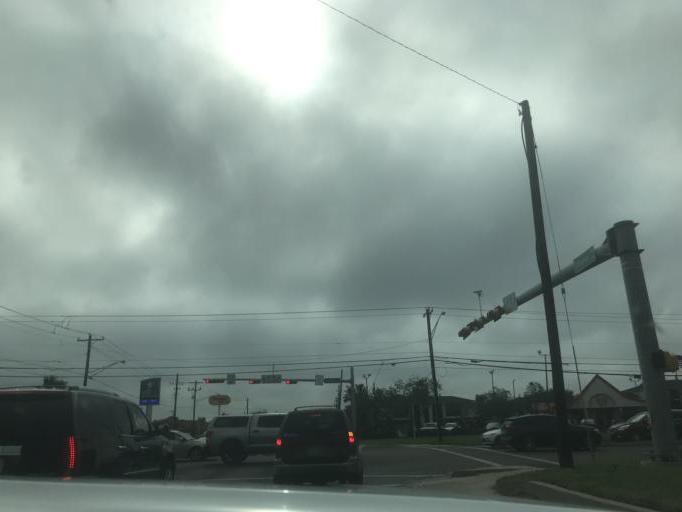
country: US
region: Texas
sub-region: Nueces County
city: Corpus Christi
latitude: 27.6787
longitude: -97.3695
